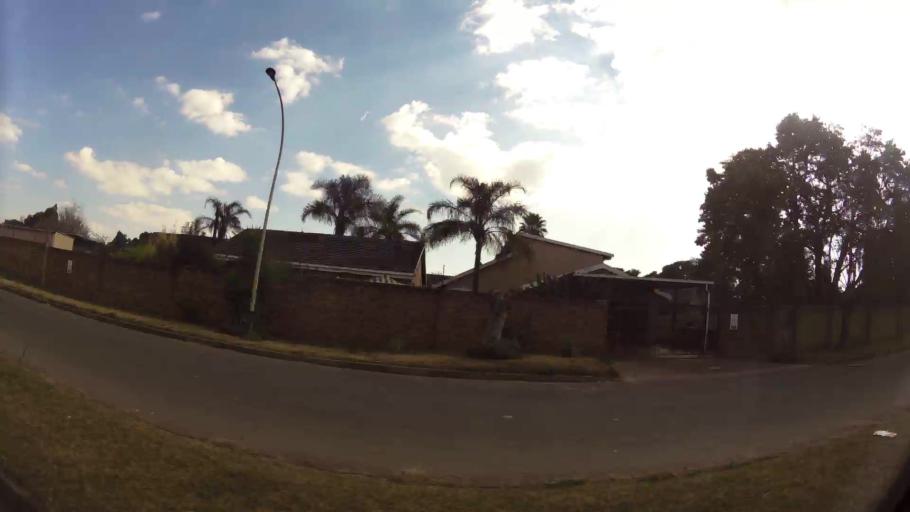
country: ZA
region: Gauteng
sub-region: Ekurhuleni Metropolitan Municipality
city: Germiston
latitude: -26.2011
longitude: 28.1439
